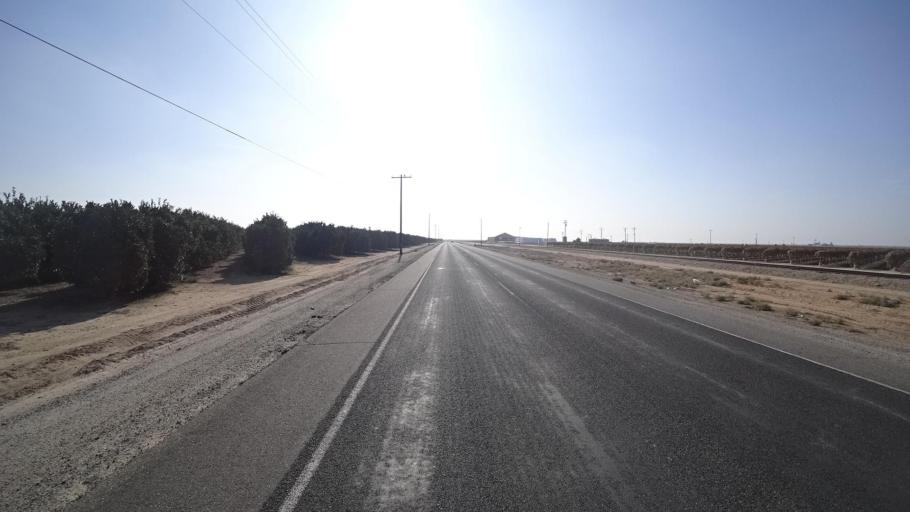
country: US
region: California
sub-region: Kern County
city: McFarland
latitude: 35.6702
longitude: -119.1893
